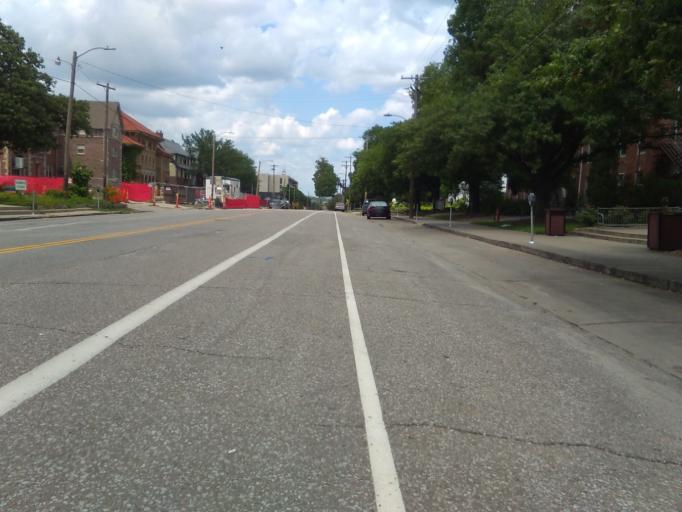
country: US
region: Nebraska
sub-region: Lancaster County
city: Lincoln
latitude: 40.8185
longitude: -96.6981
